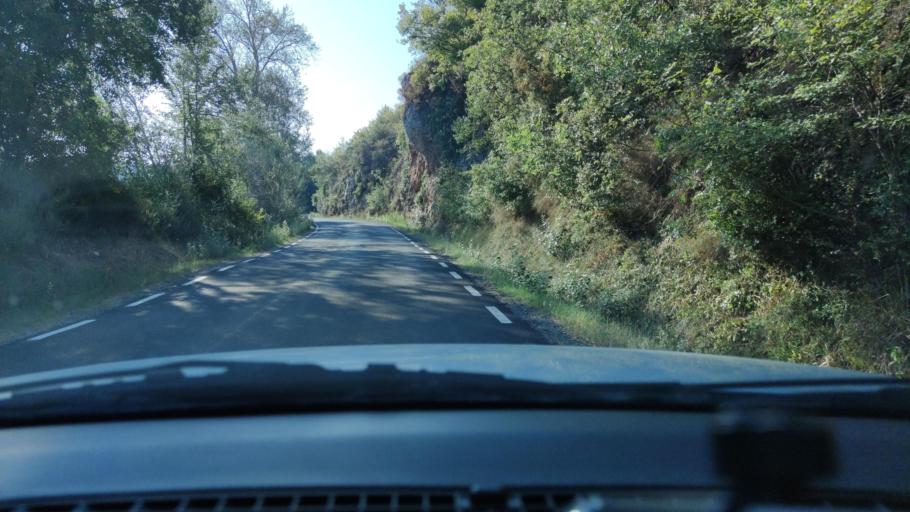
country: ES
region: Catalonia
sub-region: Provincia de Lleida
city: Camarasa
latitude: 41.8700
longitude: 0.8607
